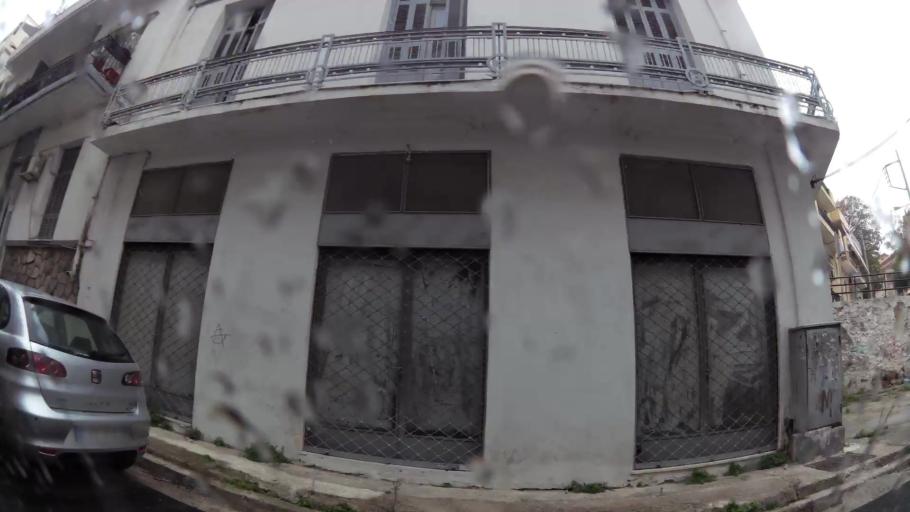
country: GR
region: Attica
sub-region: Nomos Piraios
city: Nikaia
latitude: 37.9578
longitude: 23.6478
